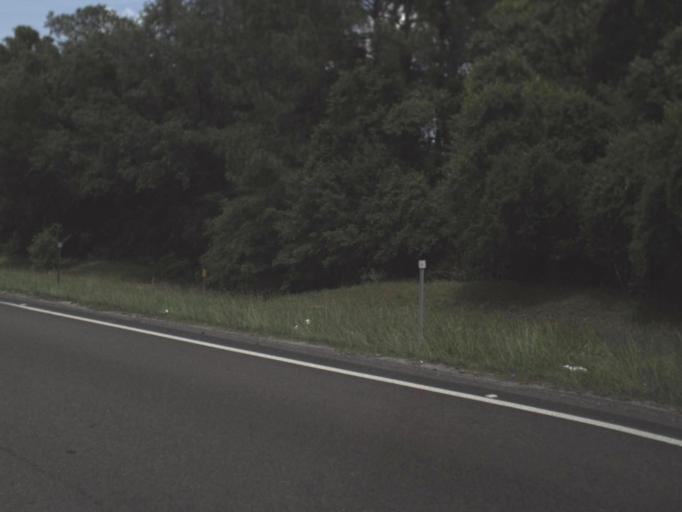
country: US
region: Florida
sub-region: Clay County
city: Bellair-Meadowbrook Terrace
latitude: 30.2519
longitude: -81.7627
